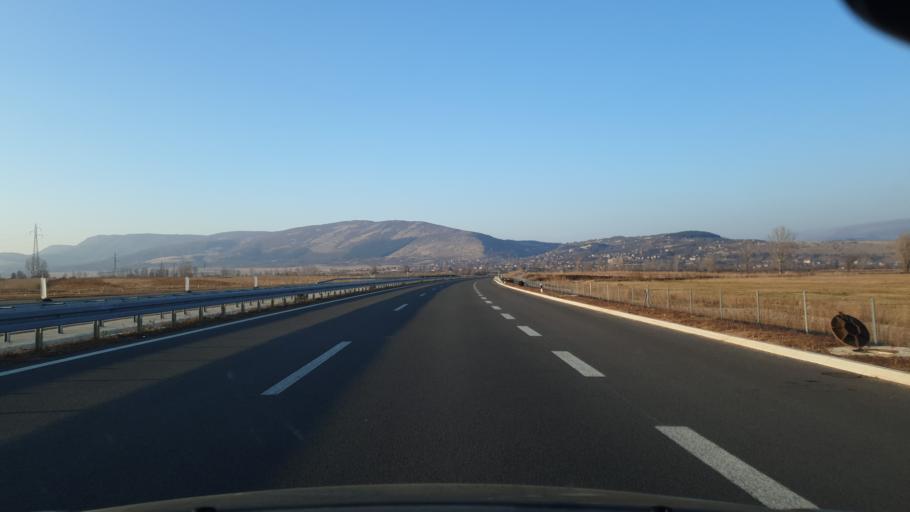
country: RS
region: Central Serbia
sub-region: Pirotski Okrug
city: Pirot
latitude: 43.1370
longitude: 22.5699
